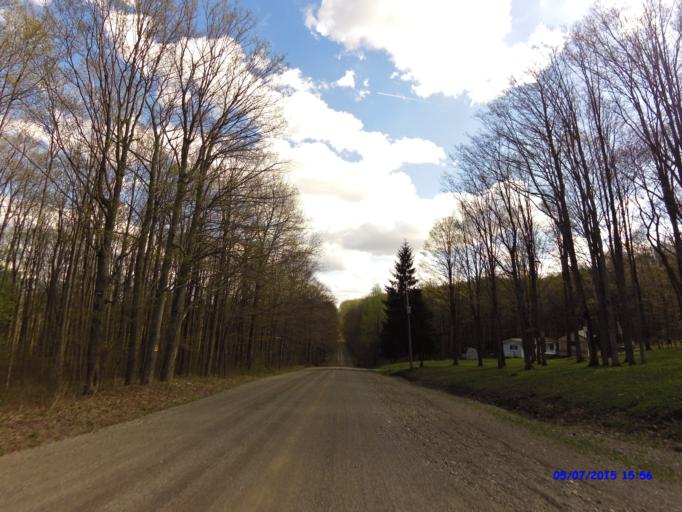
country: US
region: New York
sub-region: Cattaraugus County
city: Franklinville
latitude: 42.3102
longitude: -78.5676
